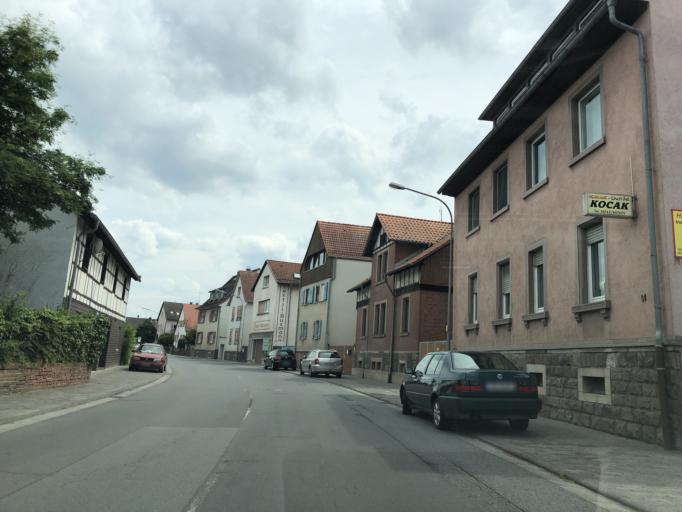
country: DE
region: Hesse
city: Gross-Bieberau
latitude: 49.7991
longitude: 8.8302
